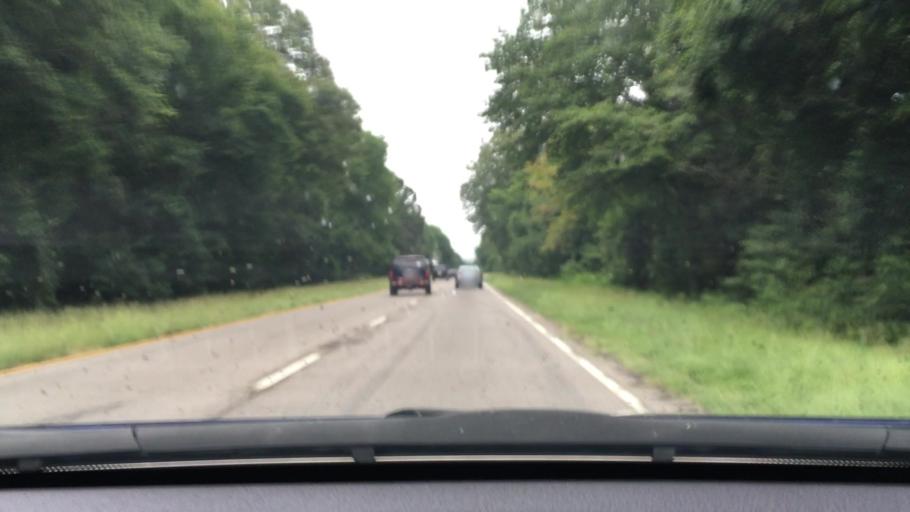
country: US
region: South Carolina
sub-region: Sumter County
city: Stateburg
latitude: 33.9509
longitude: -80.5863
